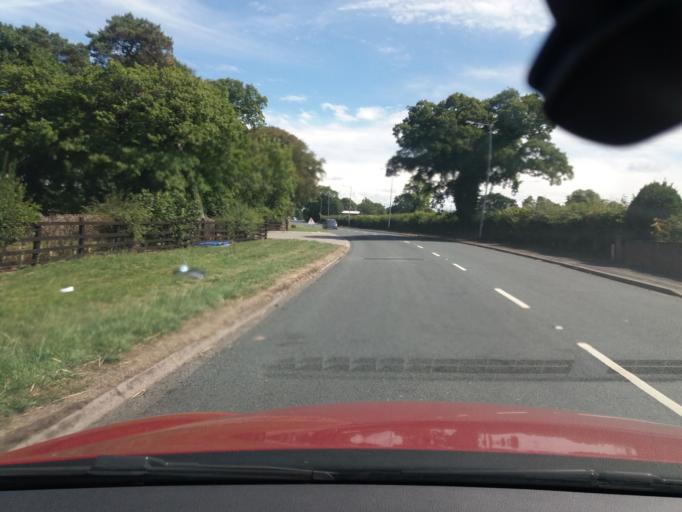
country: GB
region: England
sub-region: Lancashire
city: Euxton
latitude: 53.6594
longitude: -2.6962
